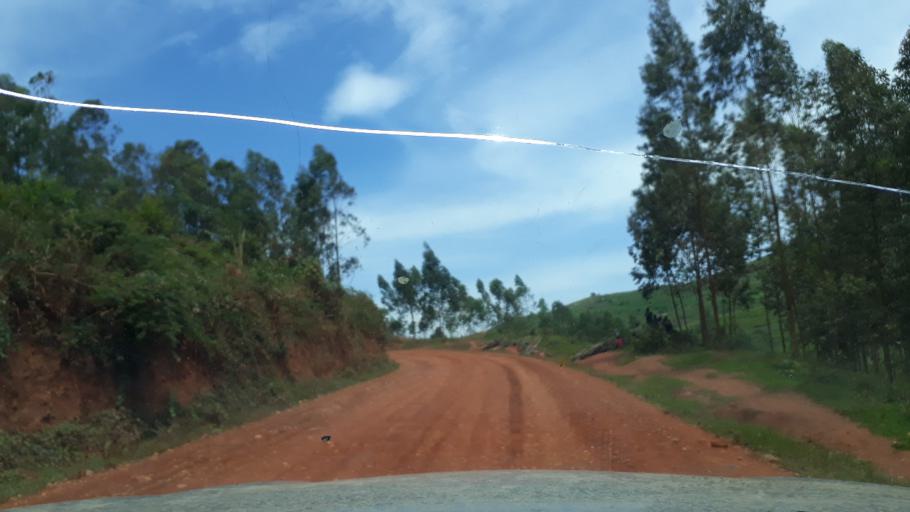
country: CD
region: Eastern Province
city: Bunia
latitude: 1.7235
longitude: 30.3121
